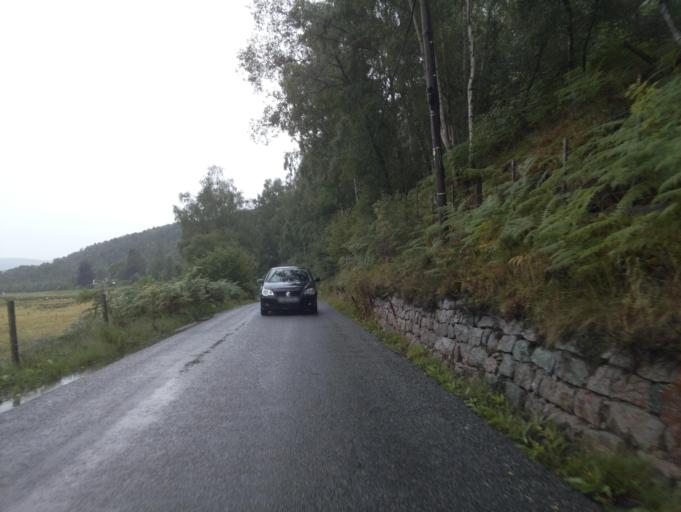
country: GB
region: Scotland
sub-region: Aberdeenshire
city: Ballater
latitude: 57.0770
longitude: -3.0879
